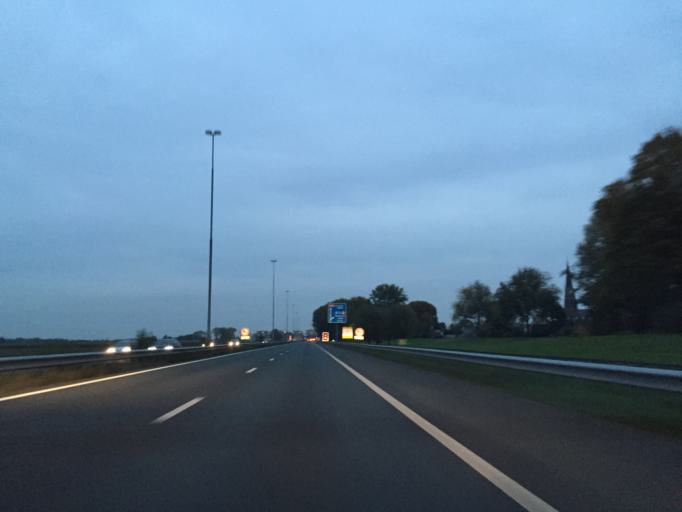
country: NL
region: North Brabant
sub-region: Gemeente Waalwijk
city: Waalwijk
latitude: 51.6948
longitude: 5.0848
